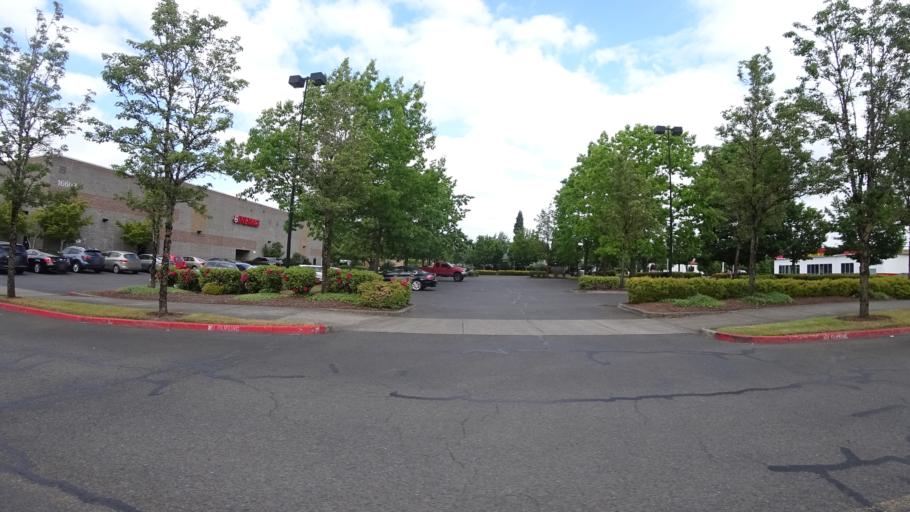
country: US
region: Oregon
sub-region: Multnomah County
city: Gresham
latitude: 45.5050
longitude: -122.4926
